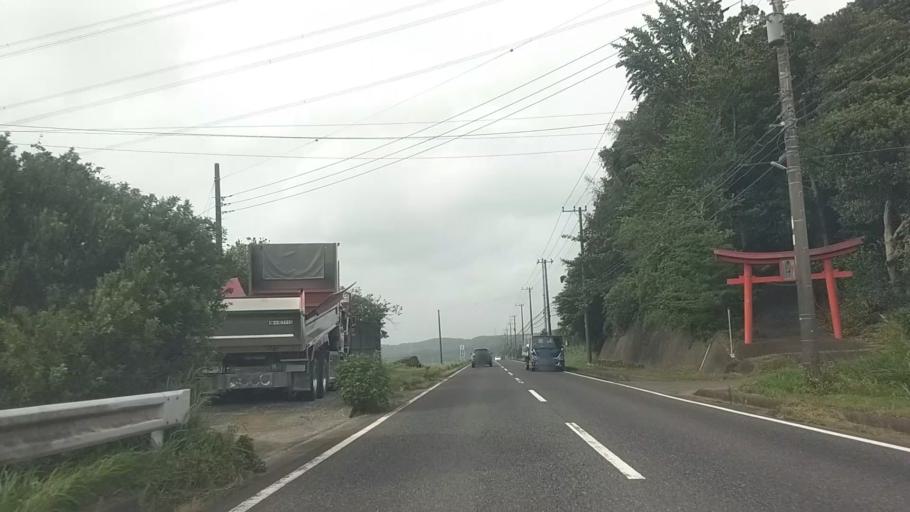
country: JP
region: Chiba
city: Kimitsu
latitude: 35.2839
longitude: 139.9902
